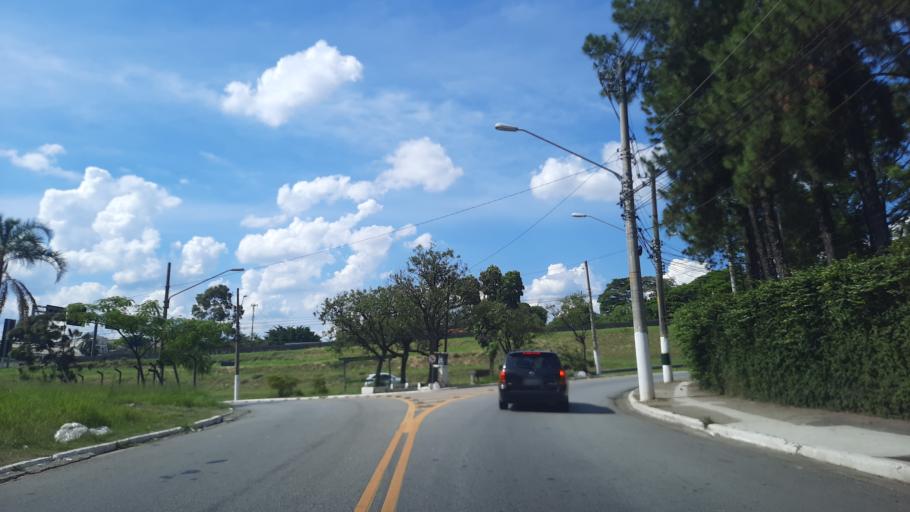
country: BR
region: Sao Paulo
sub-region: Osasco
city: Osasco
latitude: -23.5092
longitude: -46.7375
